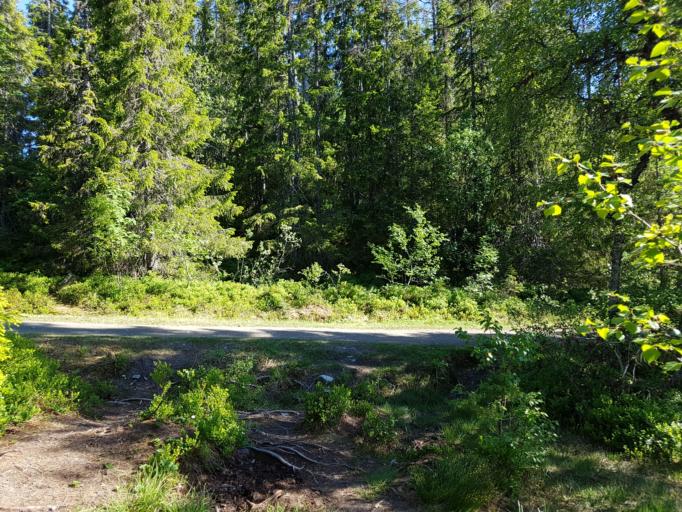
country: NO
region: Sor-Trondelag
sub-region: Trondheim
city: Trondheim
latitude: 63.4284
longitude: 10.2895
